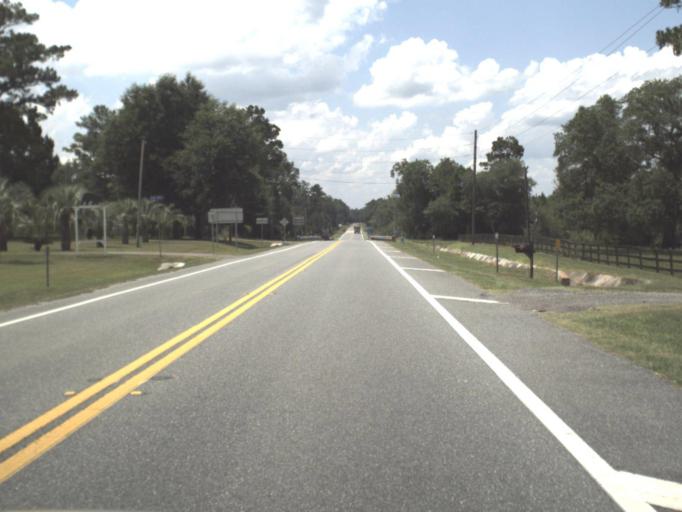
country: US
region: Florida
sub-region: Baker County
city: Macclenny
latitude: 30.3605
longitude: -82.1333
